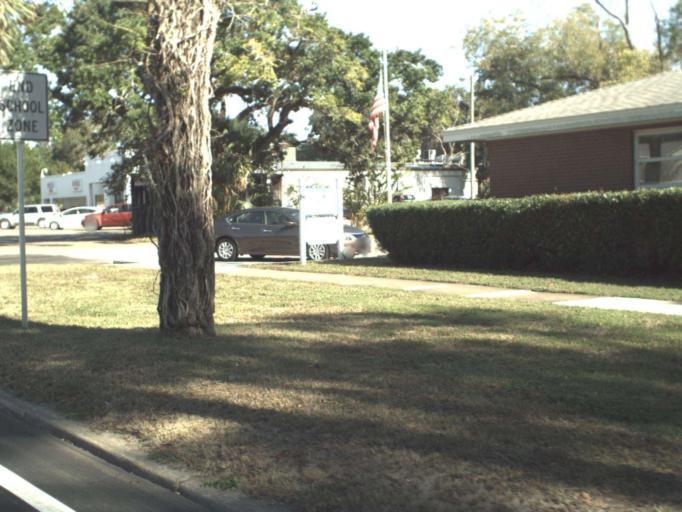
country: US
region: Florida
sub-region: Franklin County
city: Apalachicola
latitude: 29.7224
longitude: -84.9901
